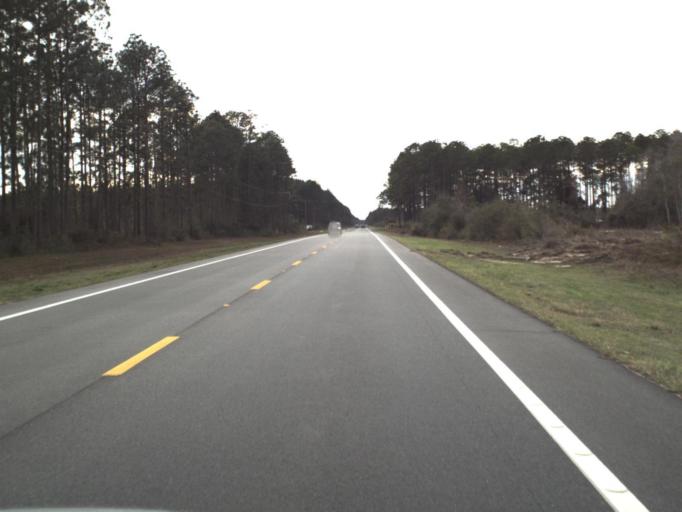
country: US
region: Florida
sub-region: Gulf County
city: Wewahitchka
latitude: 30.1408
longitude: -85.2679
